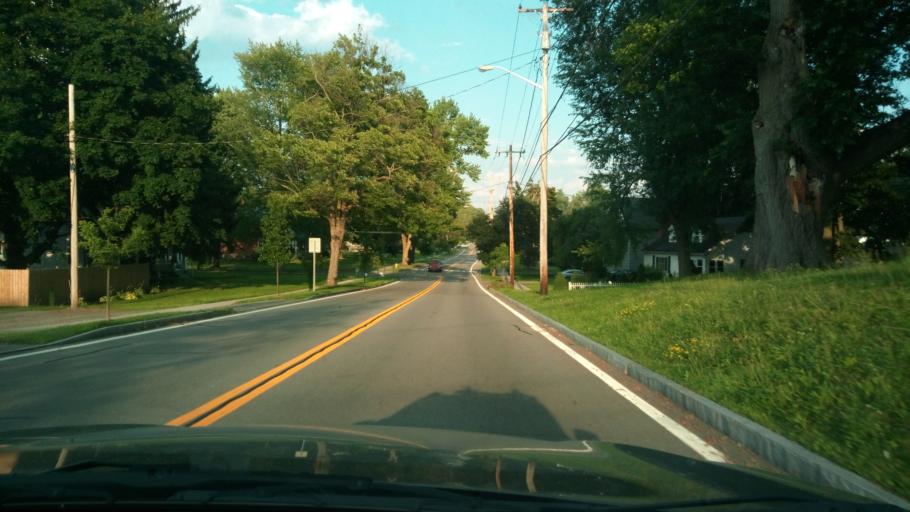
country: US
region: New York
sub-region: Wayne County
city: Clyde
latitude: 43.0868
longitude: -76.8814
